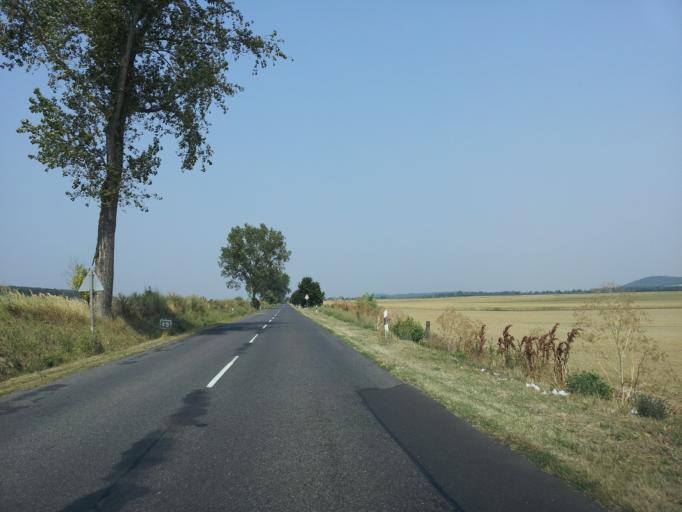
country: HU
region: Gyor-Moson-Sopron
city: Pannonhalma
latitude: 47.4734
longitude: 17.7929
